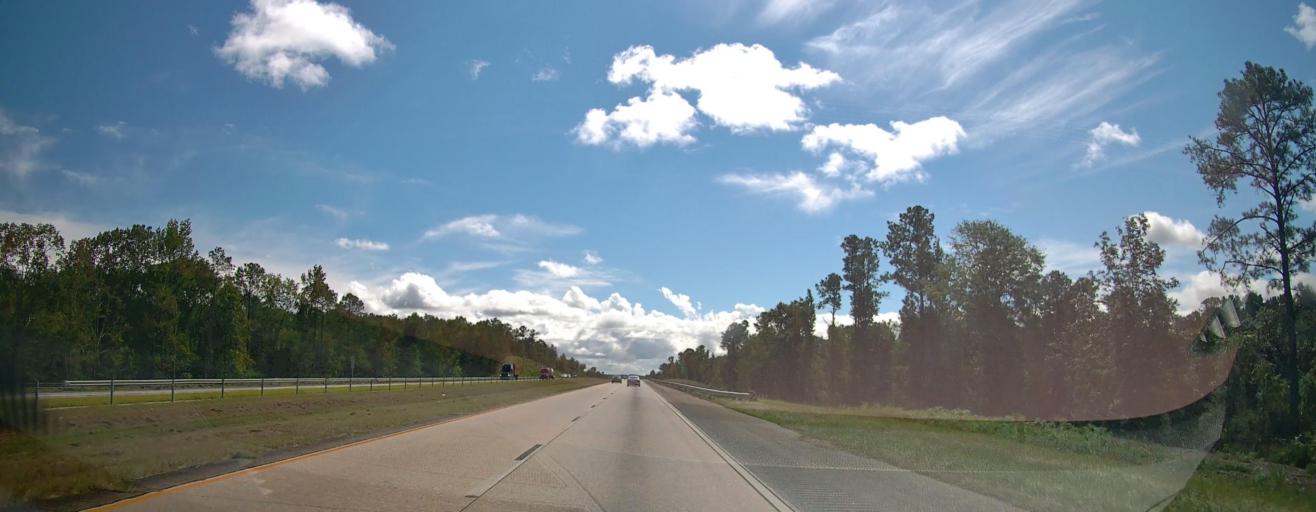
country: US
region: Georgia
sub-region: Bibb County
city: Macon
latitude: 32.7482
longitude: -83.5481
